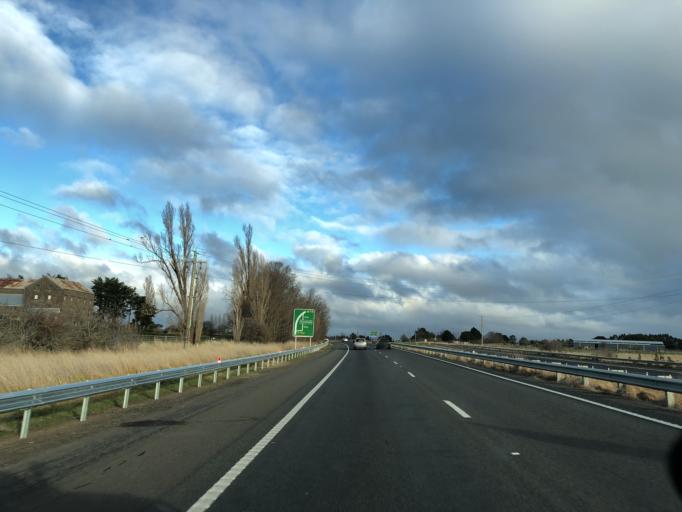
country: AU
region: Victoria
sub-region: Mount Alexander
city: Castlemaine
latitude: -37.2160
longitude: 144.4148
